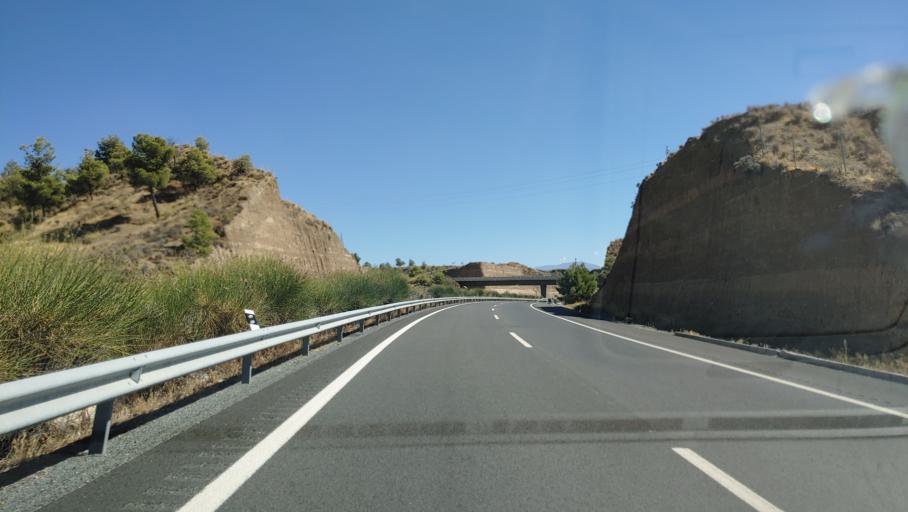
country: ES
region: Andalusia
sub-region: Provincia de Granada
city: Guadix
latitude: 37.3183
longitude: -3.1136
